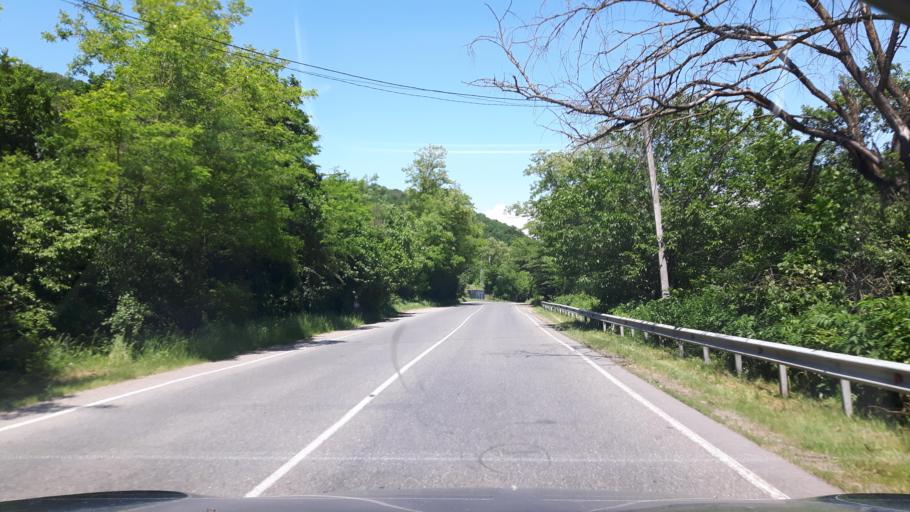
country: GE
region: Kakheti
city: Sighnaghi
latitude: 41.6398
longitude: 45.8279
